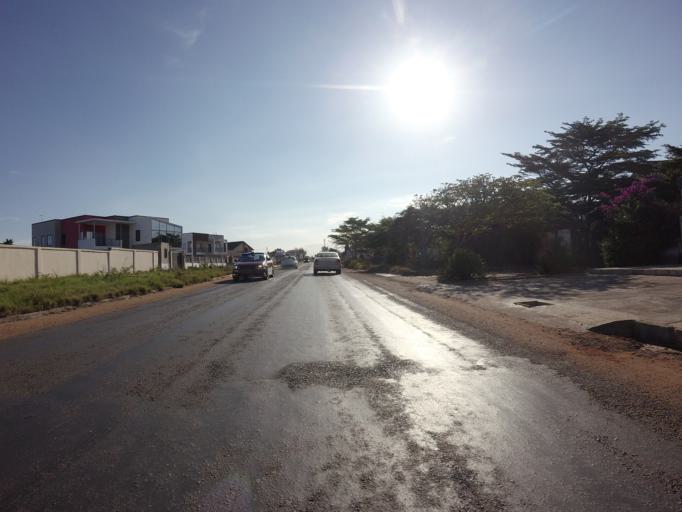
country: GH
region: Greater Accra
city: Nungua
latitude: 5.6497
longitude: -0.0732
